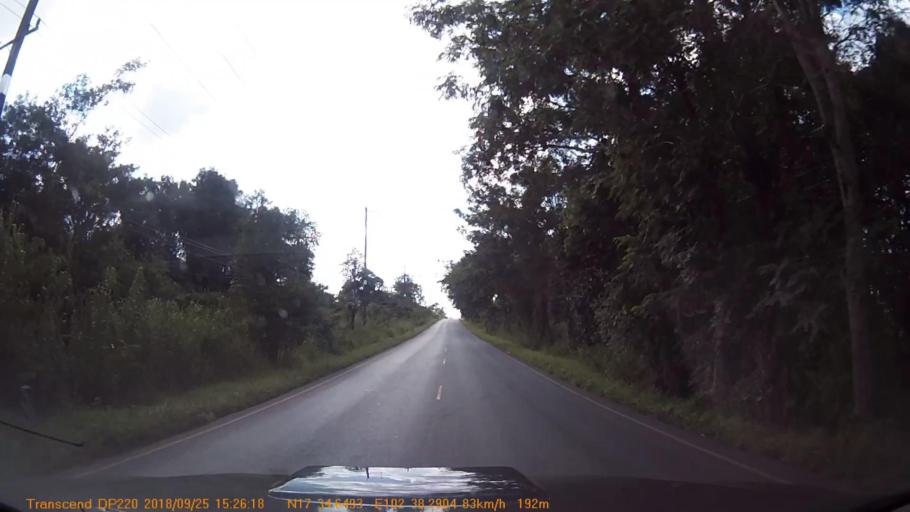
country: TH
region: Nong Khai
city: Sa Khrai
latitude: 17.5776
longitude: 102.6379
